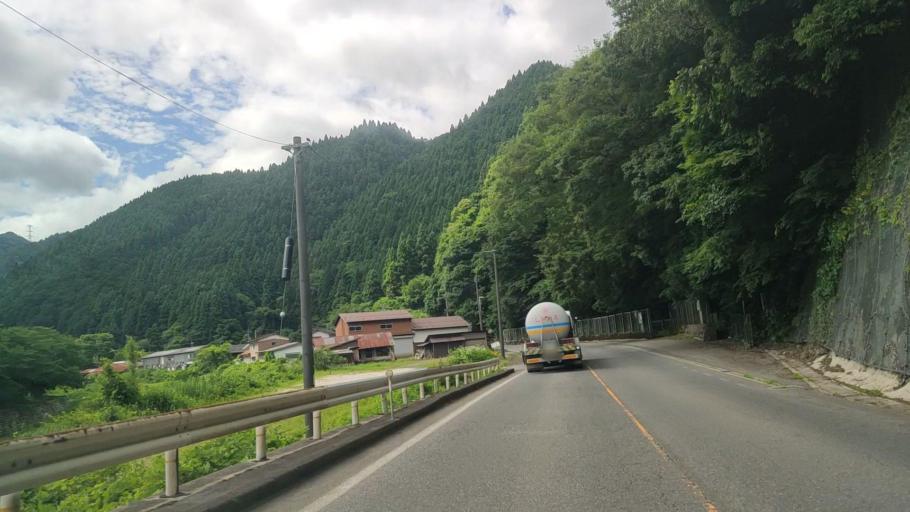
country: JP
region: Tottori
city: Yonago
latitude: 35.2347
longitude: 133.4395
